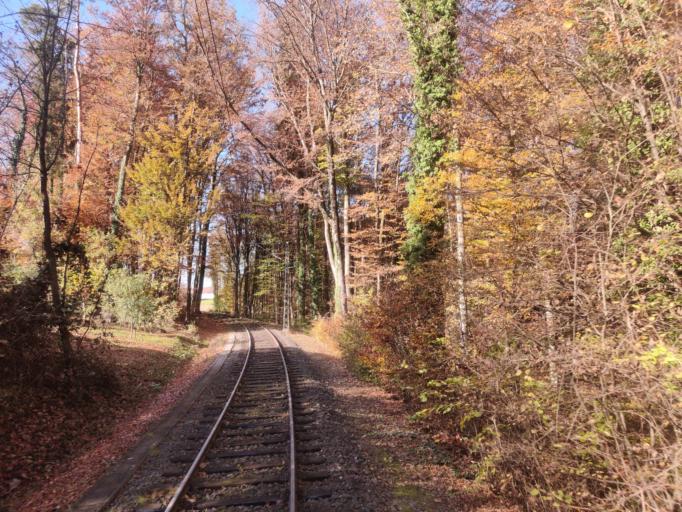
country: AT
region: Styria
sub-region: Politischer Bezirk Suedoststeiermark
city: Trautmannsdorf in Oststeiermark
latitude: 46.8776
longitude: 15.8917
